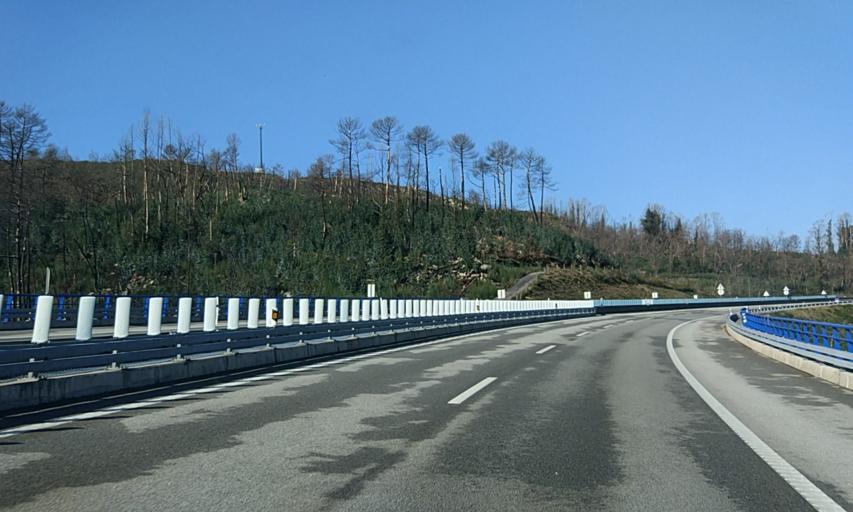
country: PT
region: Viseu
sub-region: Vouzela
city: Vouzela
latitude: 40.6976
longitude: -8.0991
